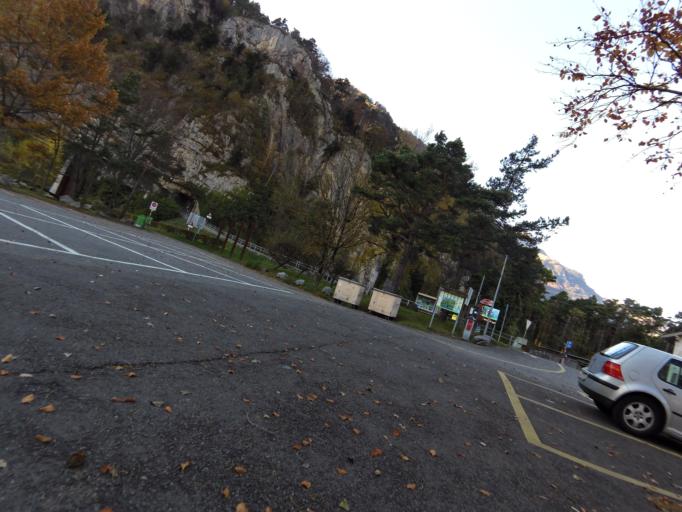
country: CH
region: Uri
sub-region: Uri
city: Bauen
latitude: 46.9173
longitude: 8.5954
